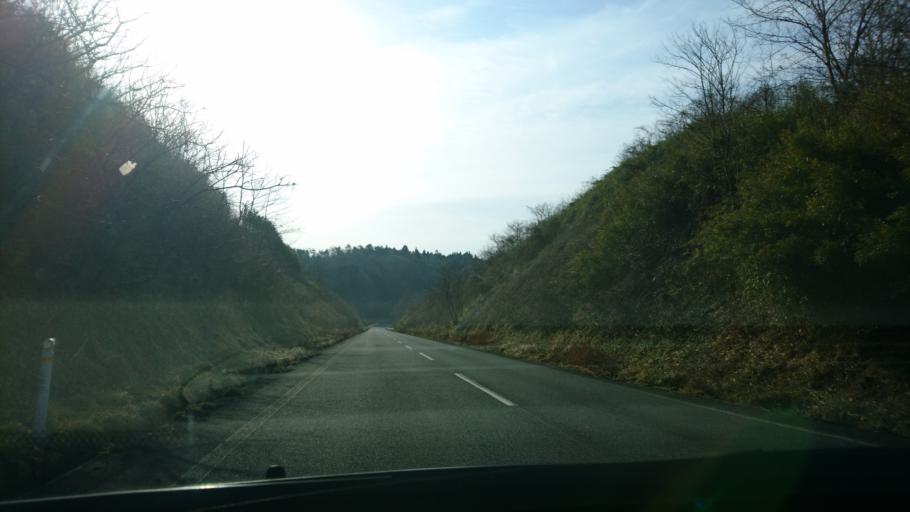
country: JP
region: Iwate
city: Ichinoseki
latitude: 38.8629
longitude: 141.1958
